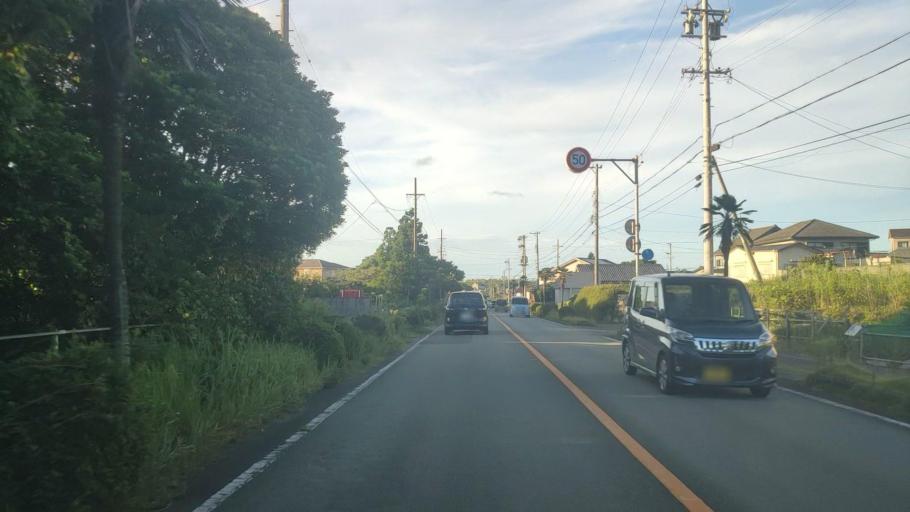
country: JP
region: Mie
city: Toba
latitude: 34.2835
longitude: 136.8819
